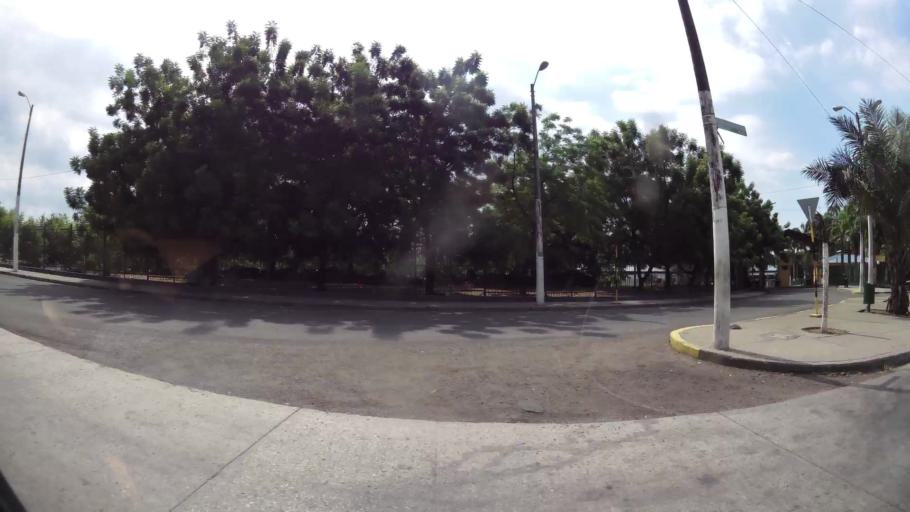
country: EC
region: Guayas
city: Santa Lucia
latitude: -2.0924
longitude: -79.9434
